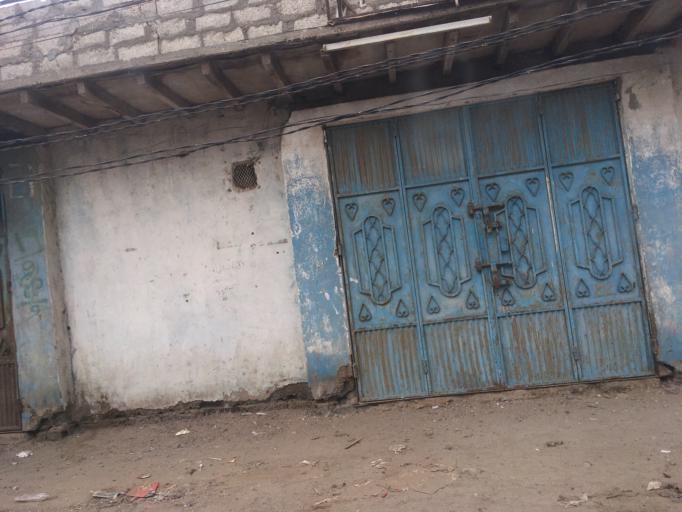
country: YE
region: Aden
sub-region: Al Mansura
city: Al Mansurah
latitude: 12.8571
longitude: 44.9945
